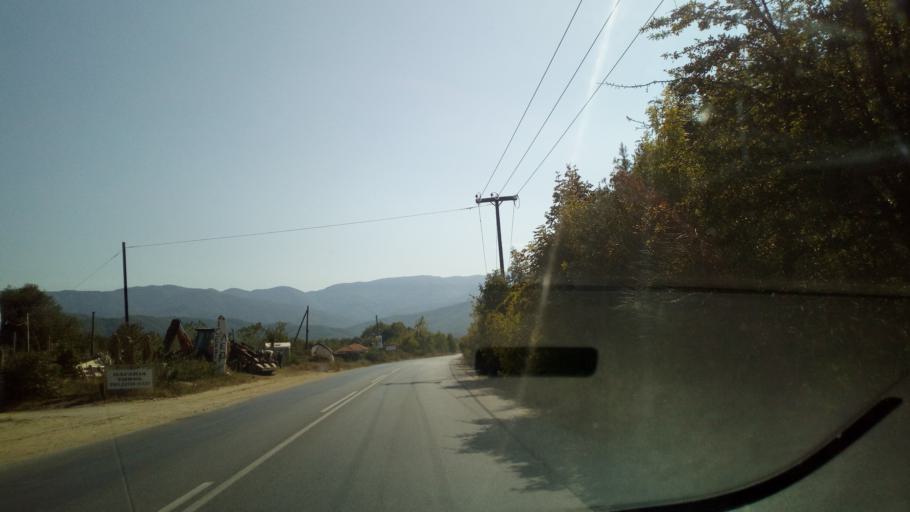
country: GR
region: Central Macedonia
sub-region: Nomos Thessalonikis
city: Stavros
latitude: 40.6074
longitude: 23.7762
